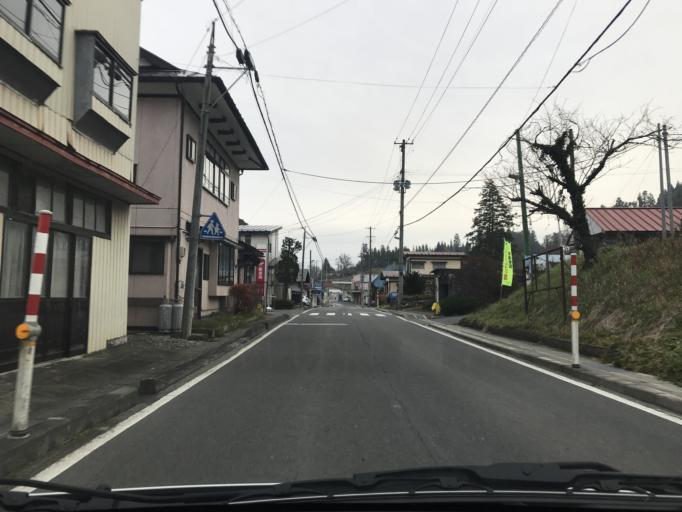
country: JP
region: Iwate
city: Kitakami
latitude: 39.2850
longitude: 141.2622
